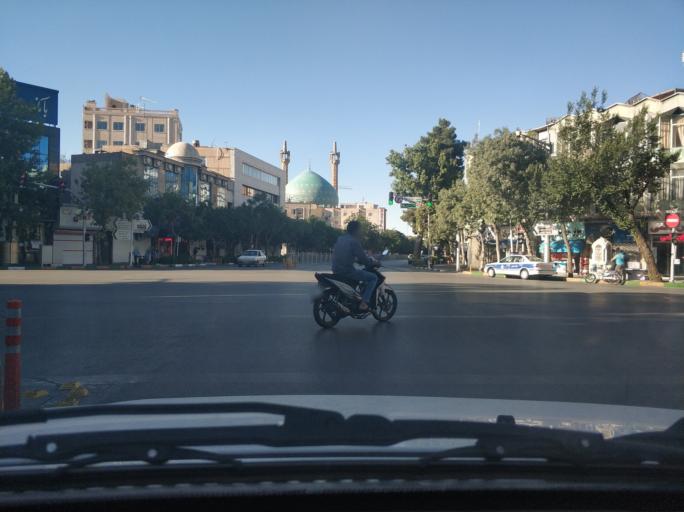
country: IR
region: Razavi Khorasan
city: Mashhad
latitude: 36.2908
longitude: 59.6062
